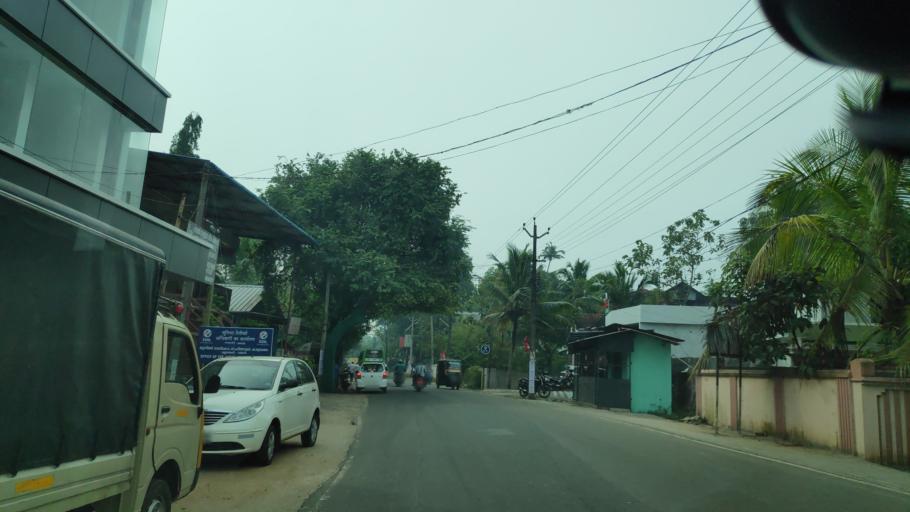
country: IN
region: Kerala
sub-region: Alappuzha
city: Alleppey
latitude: 9.5712
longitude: 76.3475
